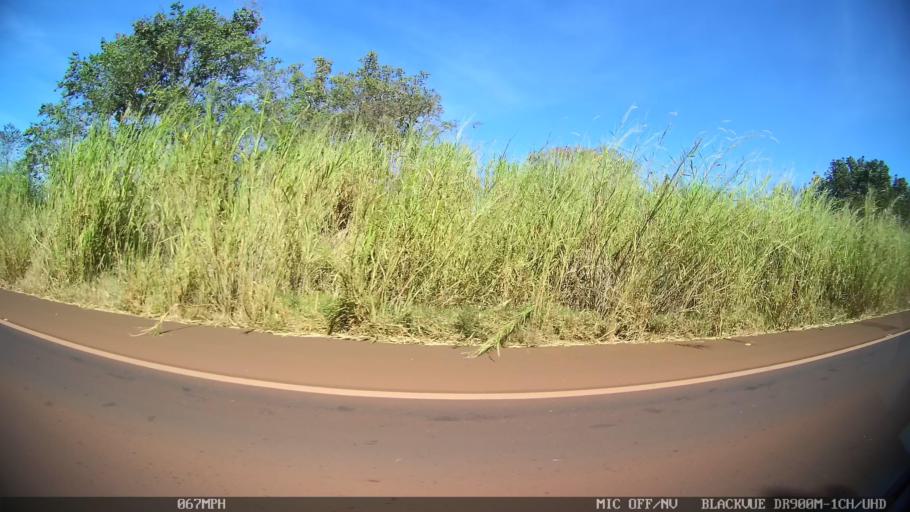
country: BR
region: Sao Paulo
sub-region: Sao Joaquim Da Barra
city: Sao Joaquim da Barra
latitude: -20.5531
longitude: -47.6766
